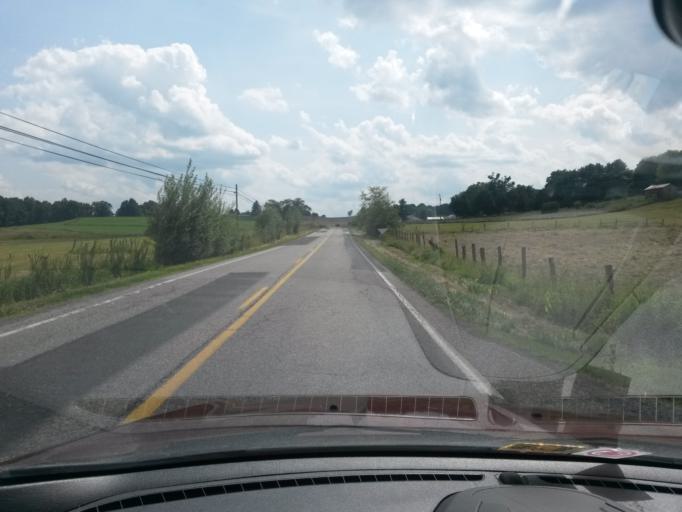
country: US
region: Virginia
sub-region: Highland County
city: Monterey
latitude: 38.4222
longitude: -79.5700
